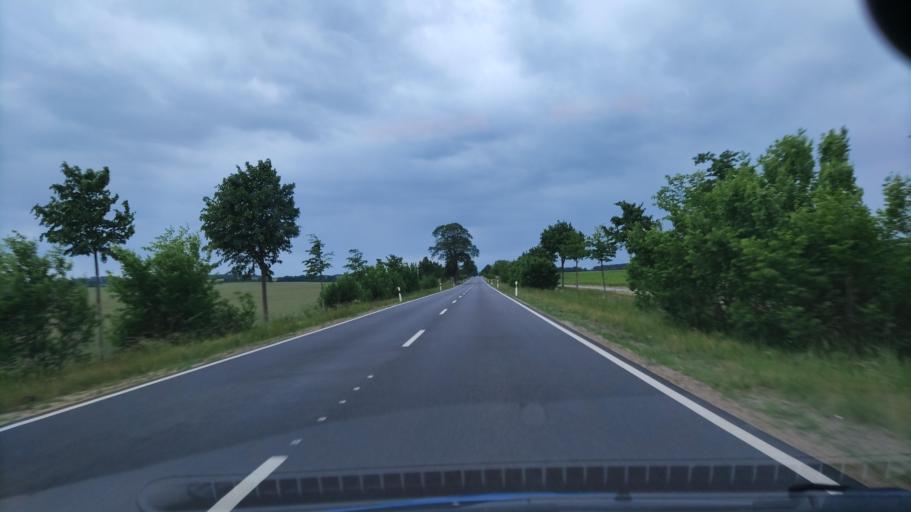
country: DE
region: Mecklenburg-Vorpommern
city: Spornitz
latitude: 53.4185
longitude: 11.7695
